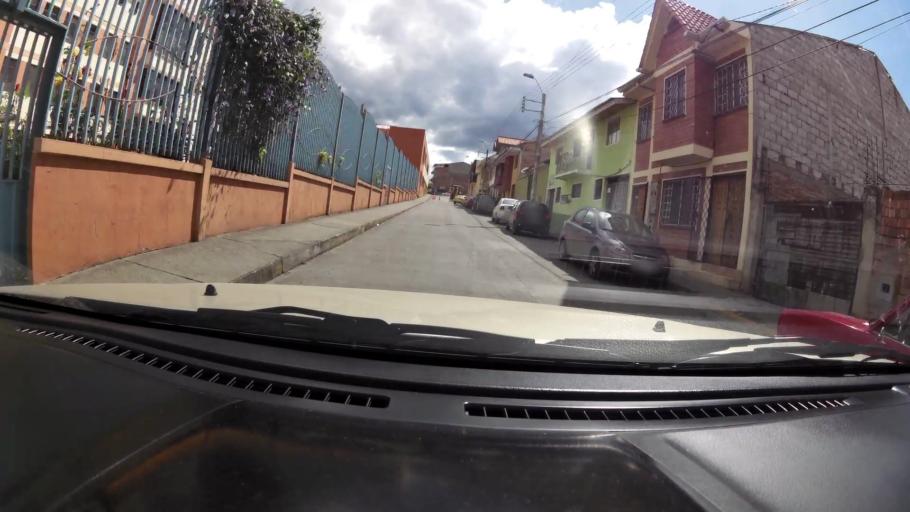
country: EC
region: Azuay
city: Cuenca
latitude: -2.8858
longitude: -78.9909
